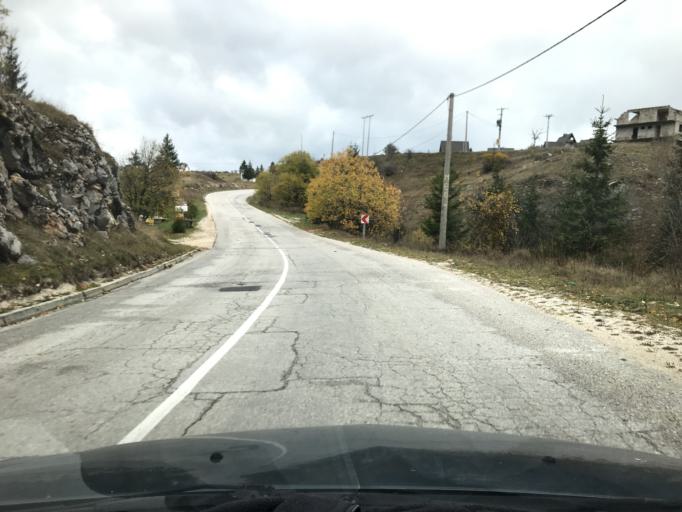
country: BA
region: Federation of Bosnia and Herzegovina
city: Turbe
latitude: 44.3096
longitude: 17.5489
